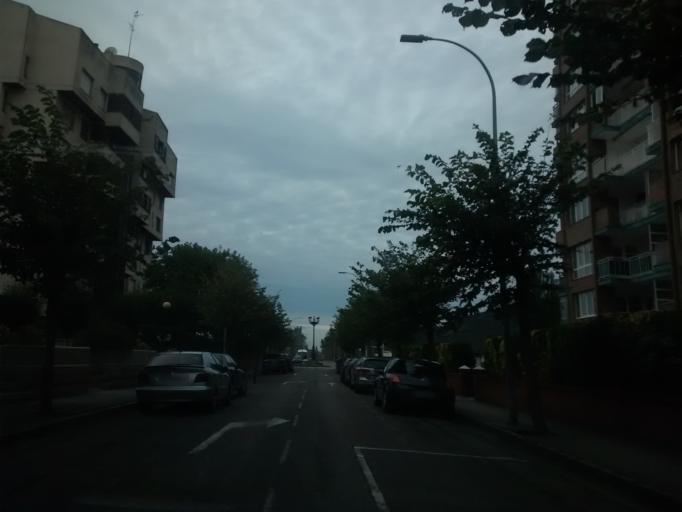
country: ES
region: Cantabria
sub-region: Provincia de Cantabria
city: Santona
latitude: 43.4279
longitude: -3.4482
